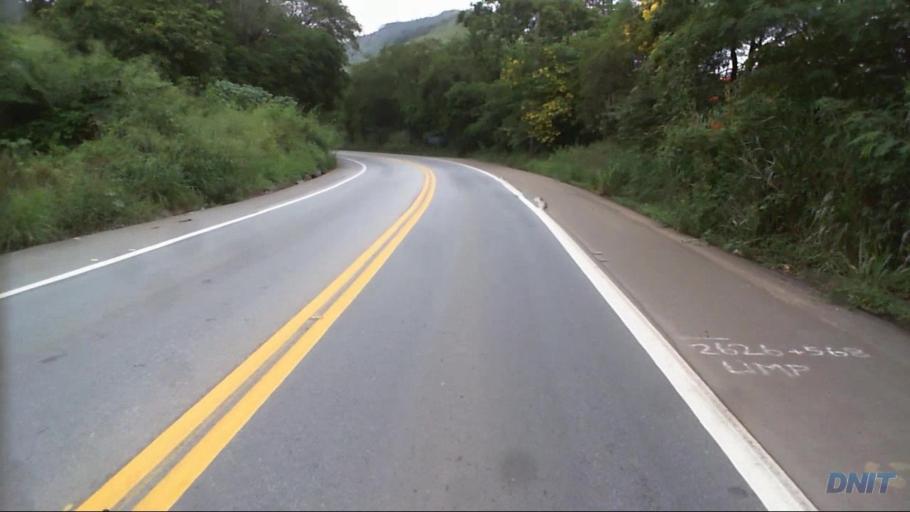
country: BR
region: Minas Gerais
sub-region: Timoteo
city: Timoteo
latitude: -19.5690
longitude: -42.7127
